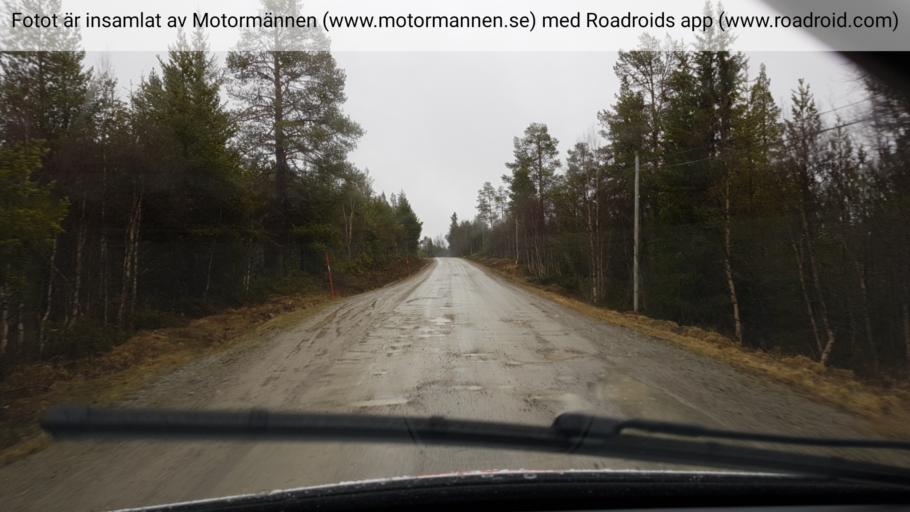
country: SE
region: Jaemtland
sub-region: Are Kommun
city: Jarpen
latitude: 62.5551
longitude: 13.4328
